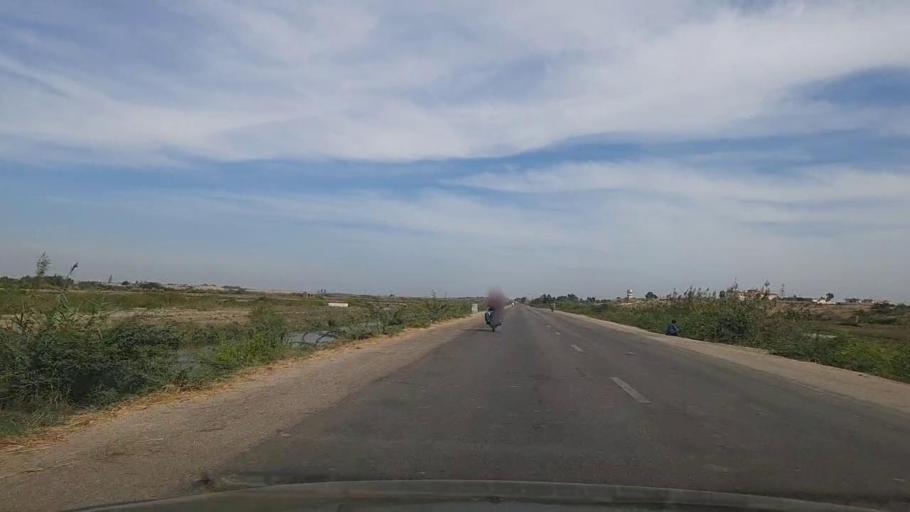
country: PK
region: Sindh
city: Thatta
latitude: 24.8147
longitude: 67.9796
